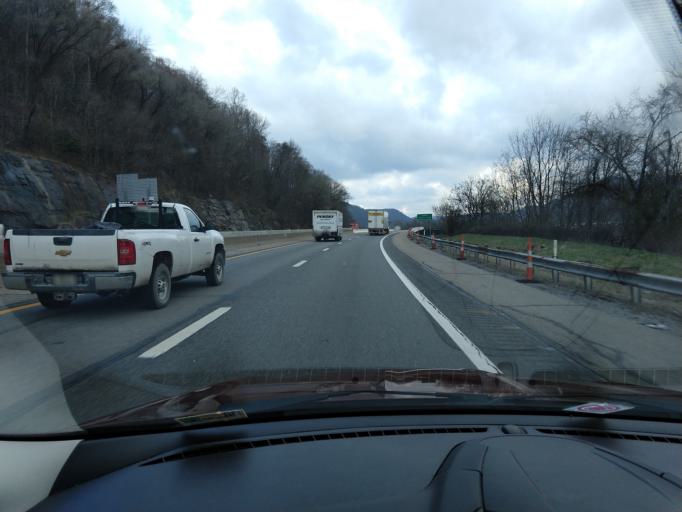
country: US
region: West Virginia
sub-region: Kanawha County
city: Marmet
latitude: 38.2549
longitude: -81.5730
